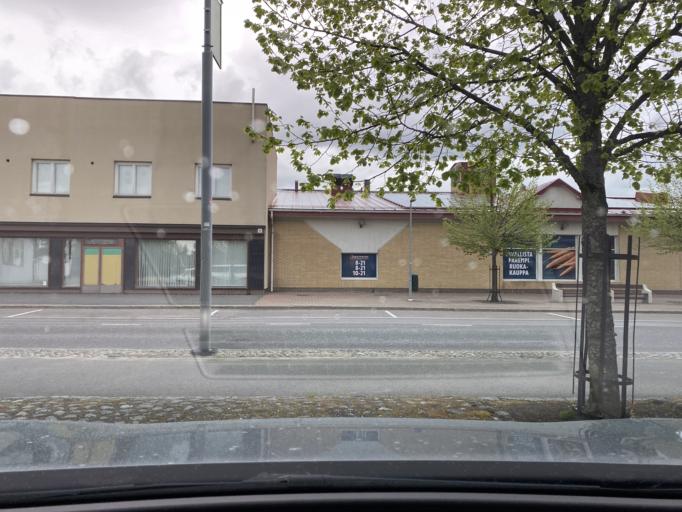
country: FI
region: Varsinais-Suomi
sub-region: Salo
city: Somero
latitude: 60.6263
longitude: 23.5170
